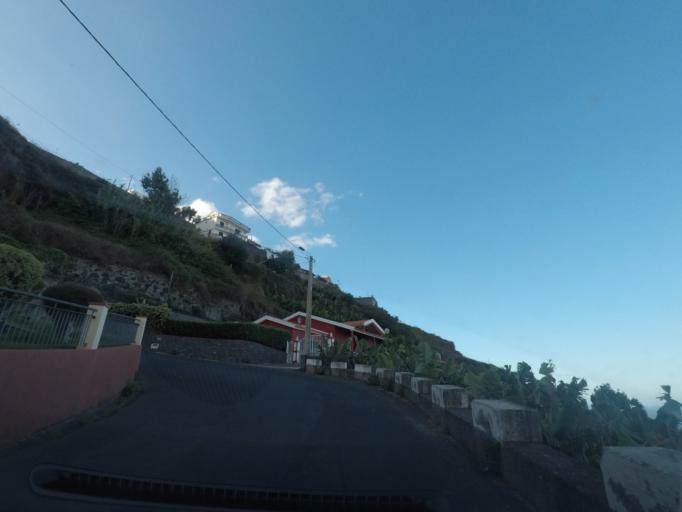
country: PT
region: Madeira
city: Ponta do Sol
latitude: 32.6862
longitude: -17.0924
